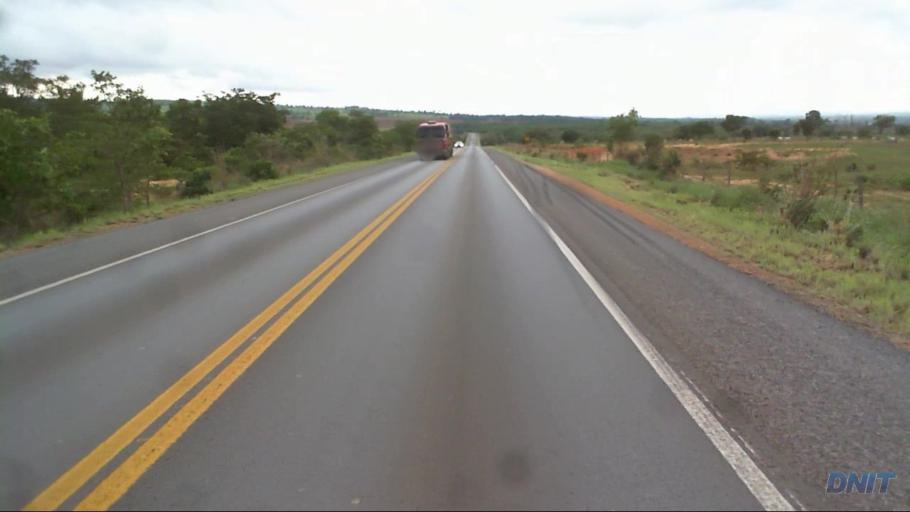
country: BR
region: Goias
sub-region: Padre Bernardo
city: Padre Bernardo
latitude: -15.2128
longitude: -48.5608
